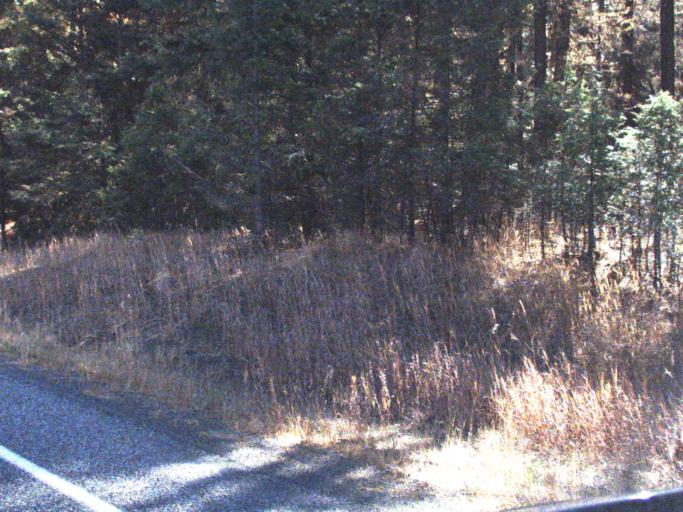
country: US
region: Washington
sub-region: Ferry County
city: Republic
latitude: 48.6559
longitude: -118.8072
